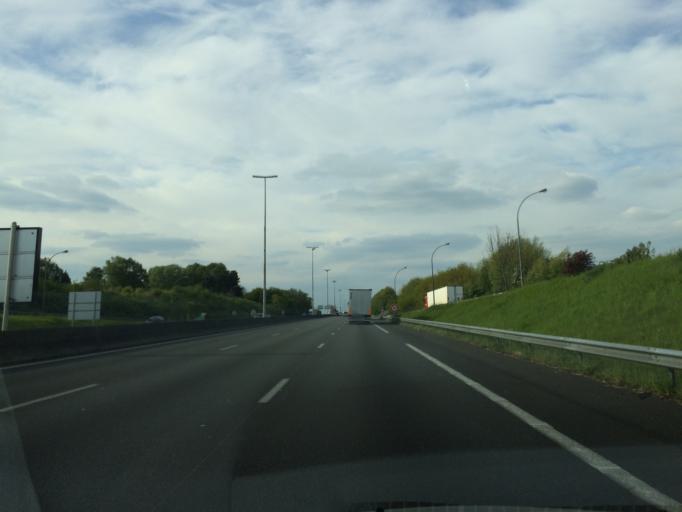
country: FR
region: Ile-de-France
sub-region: Departement du Val-d'Oise
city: Survilliers
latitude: 49.0869
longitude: 2.5511
